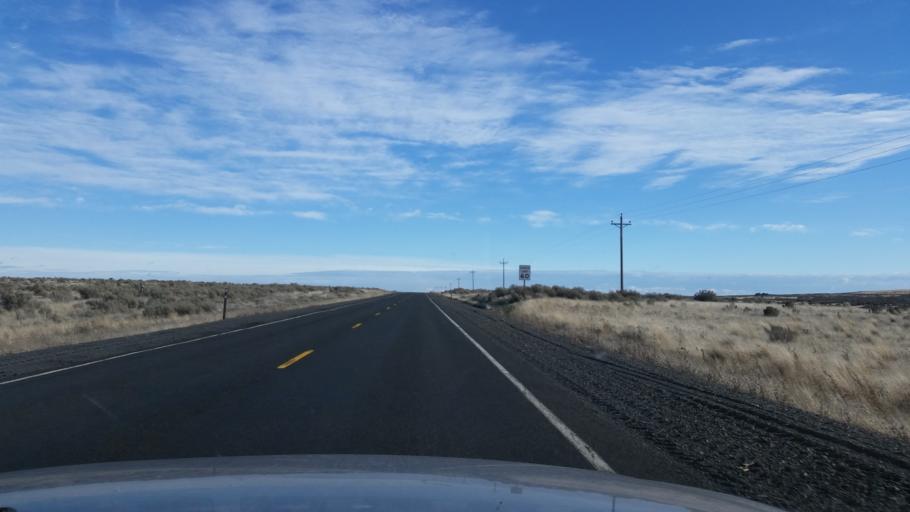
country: US
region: Washington
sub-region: Grant County
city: Warden
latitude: 47.3153
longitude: -118.8065
